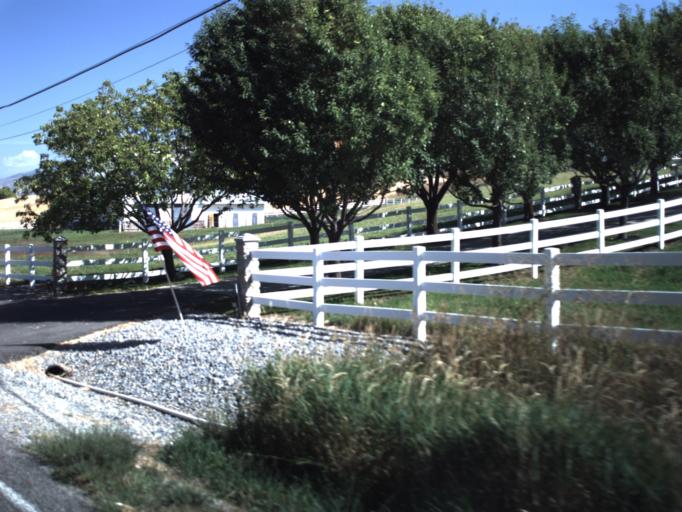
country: US
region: Utah
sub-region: Cache County
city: Hyrum
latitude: 41.5816
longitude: -111.8386
